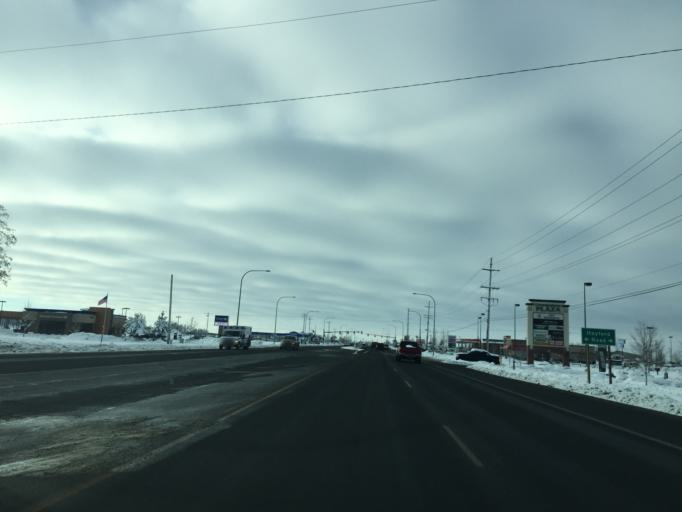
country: US
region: Washington
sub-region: Spokane County
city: Airway Heights
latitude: 47.6431
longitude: -117.5570
